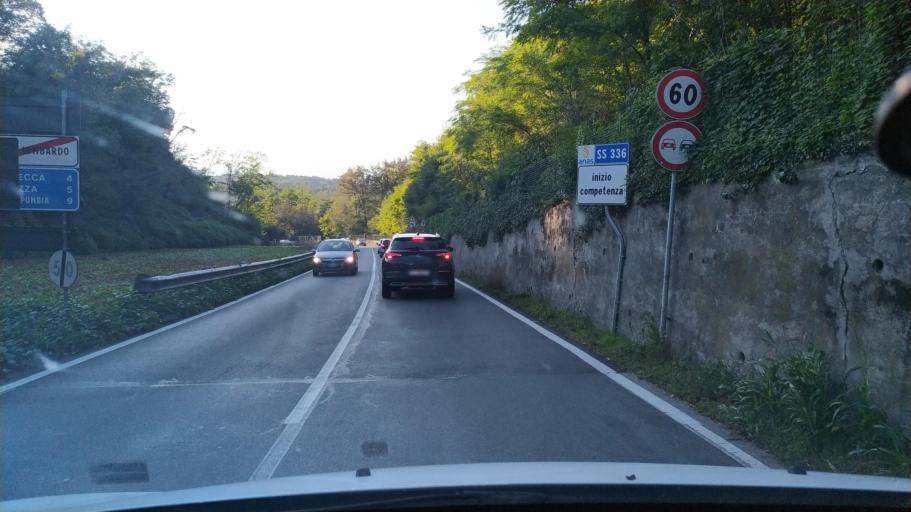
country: IT
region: Lombardy
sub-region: Provincia di Varese
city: Somma Lombardo
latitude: 45.6900
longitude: 8.6937
